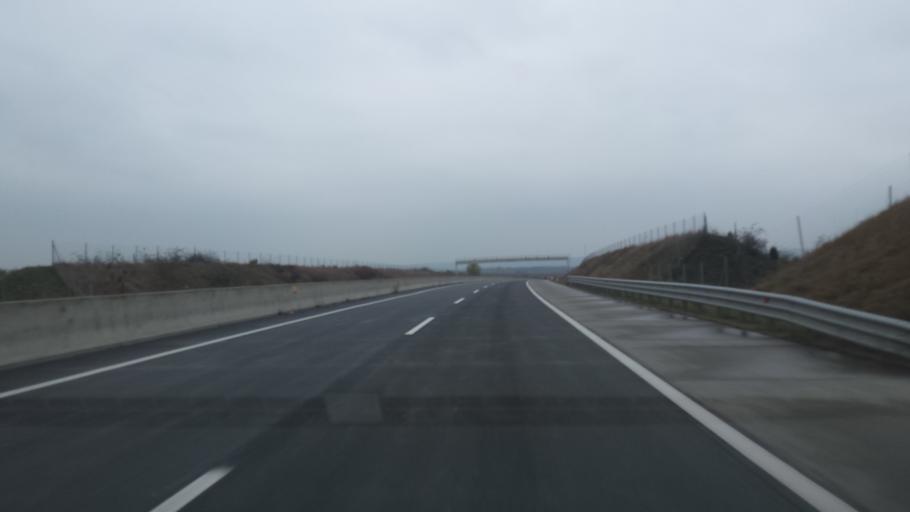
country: AT
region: Lower Austria
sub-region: Politischer Bezirk Mistelbach
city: Hochleithen
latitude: 48.4569
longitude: 16.5525
